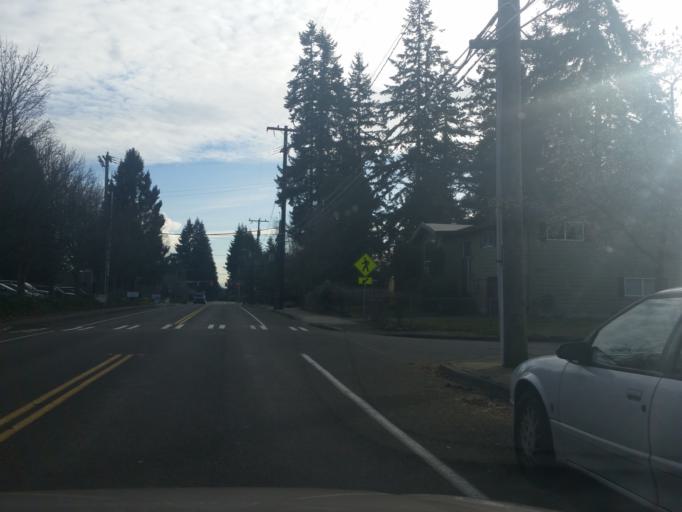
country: US
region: Washington
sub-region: King County
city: Shoreline
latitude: 47.7652
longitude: -122.3297
